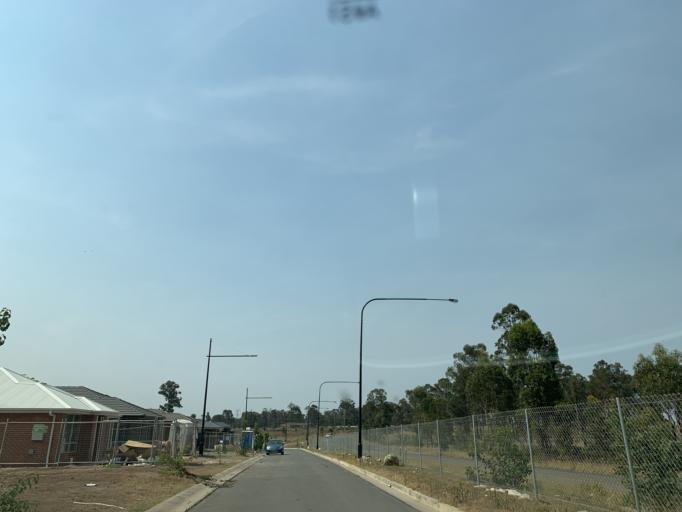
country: AU
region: New South Wales
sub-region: Blacktown
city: Blackett
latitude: -33.7137
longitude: 150.8206
